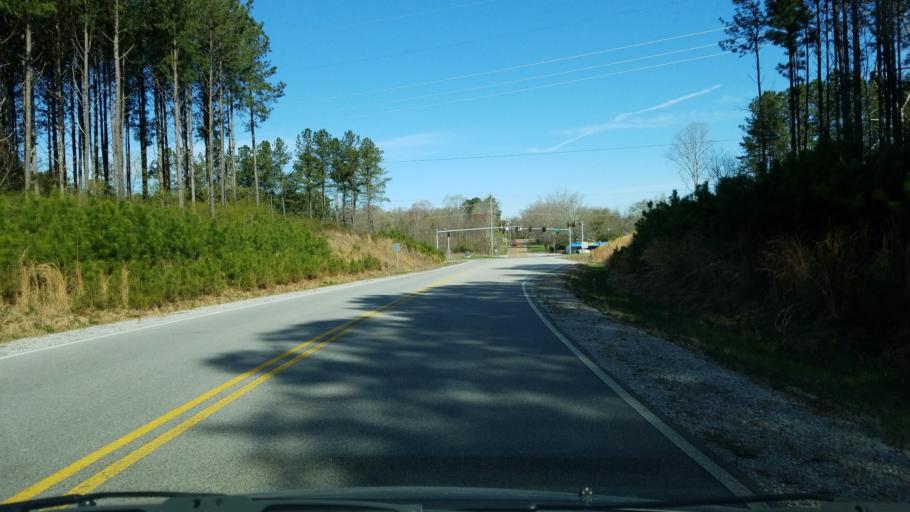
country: US
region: Tennessee
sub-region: Hamilton County
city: Harrison
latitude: 35.1068
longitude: -85.1445
